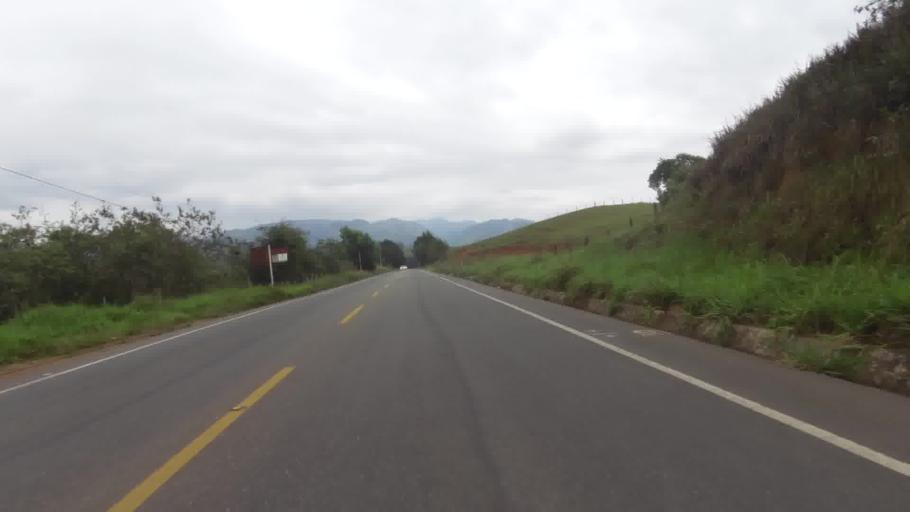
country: BR
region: Espirito Santo
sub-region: Iconha
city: Iconha
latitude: -20.7805
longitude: -40.7567
